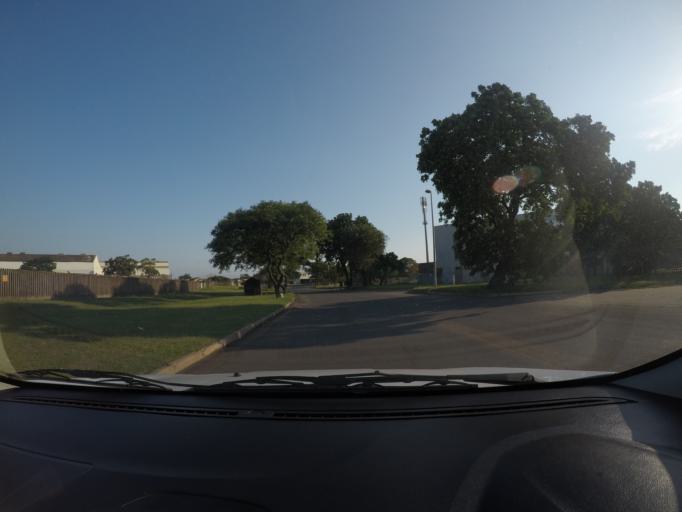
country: ZA
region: KwaZulu-Natal
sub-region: uThungulu District Municipality
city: Richards Bay
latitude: -28.7687
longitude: 32.0096
